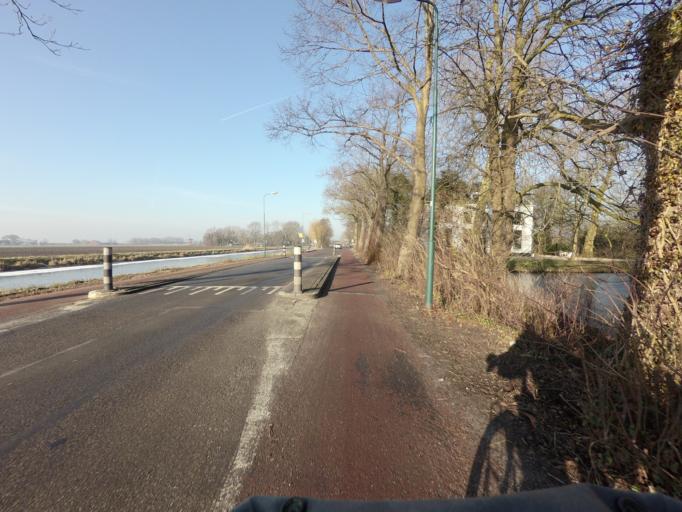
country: NL
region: Utrecht
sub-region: Stichtse Vecht
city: Vreeland
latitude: 52.2542
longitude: 4.9928
